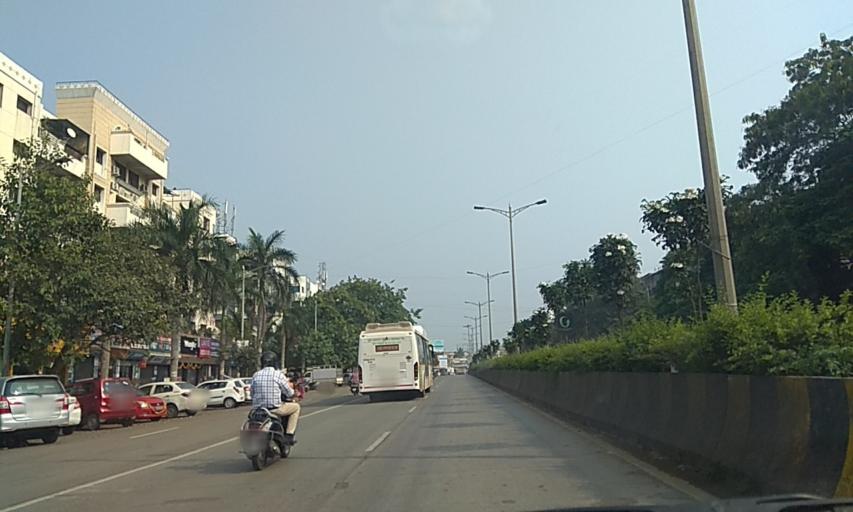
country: IN
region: Maharashtra
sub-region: Pune Division
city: Lohogaon
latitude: 18.5594
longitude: 73.9383
